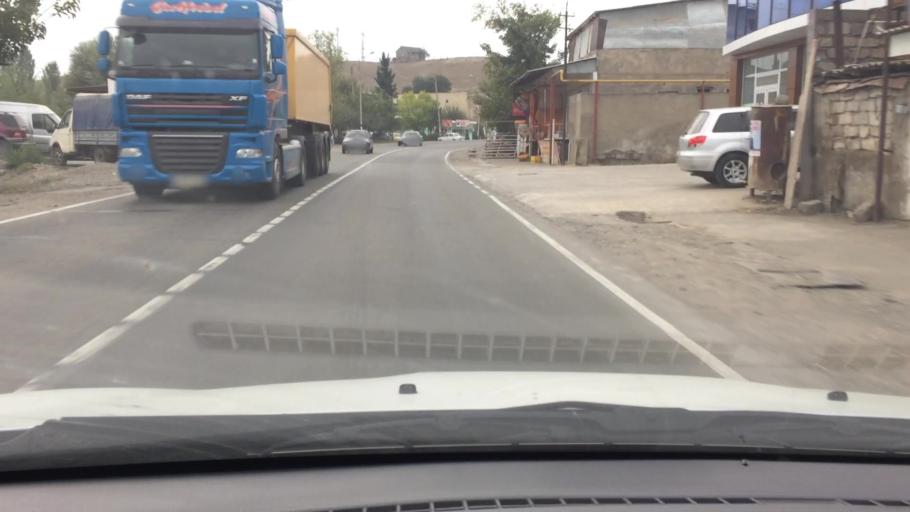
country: GE
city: Naghvarevi
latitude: 41.3666
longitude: 44.8404
